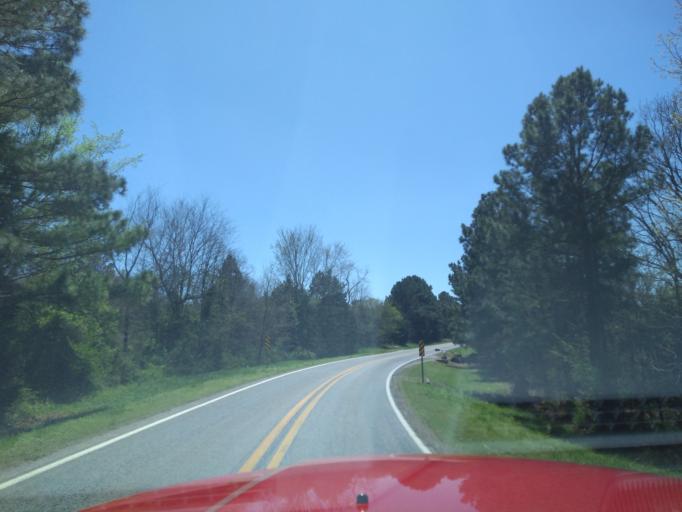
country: US
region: Arkansas
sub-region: Washington County
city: West Fork
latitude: 35.8328
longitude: -94.2670
